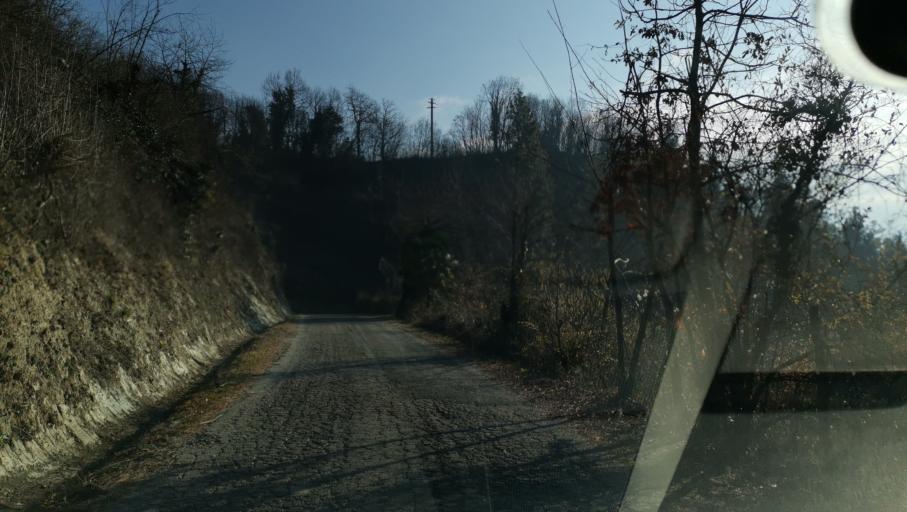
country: IT
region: Piedmont
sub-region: Provincia di Torino
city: Rivalba
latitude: 45.1318
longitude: 7.8946
